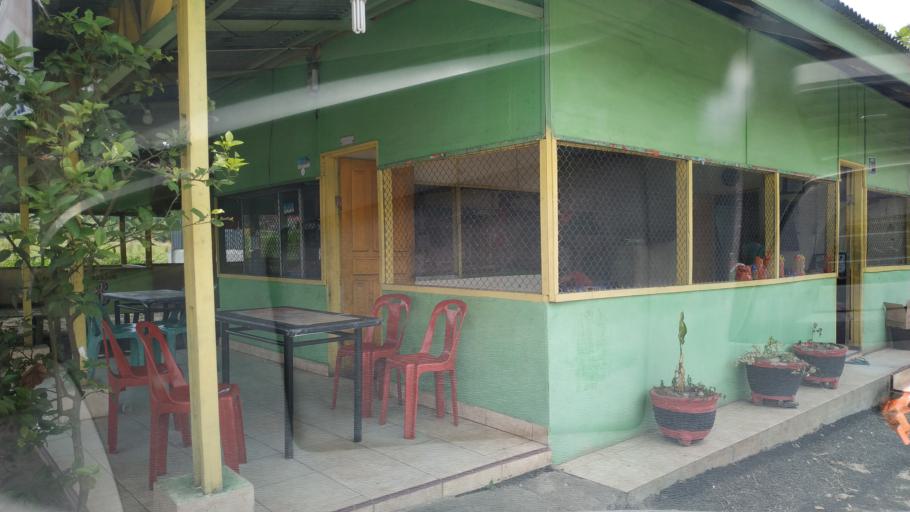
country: ID
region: North Sumatra
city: Langgapayung
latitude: 1.7160
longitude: 99.9228
